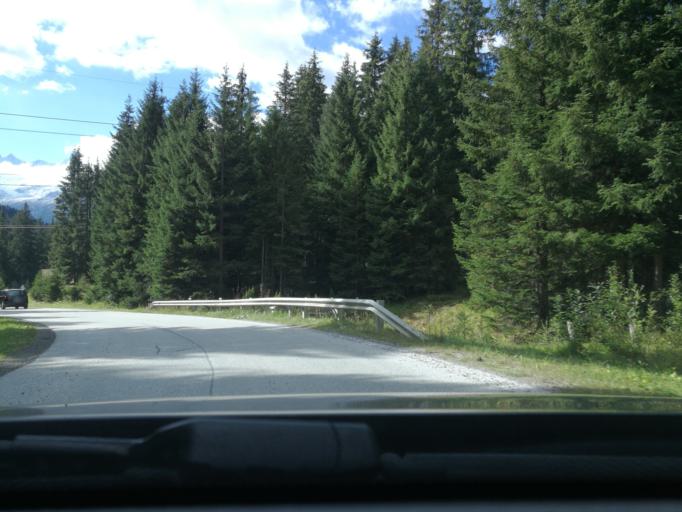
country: AT
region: Salzburg
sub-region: Politischer Bezirk Zell am See
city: Krimml
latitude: 47.2466
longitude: 12.1178
